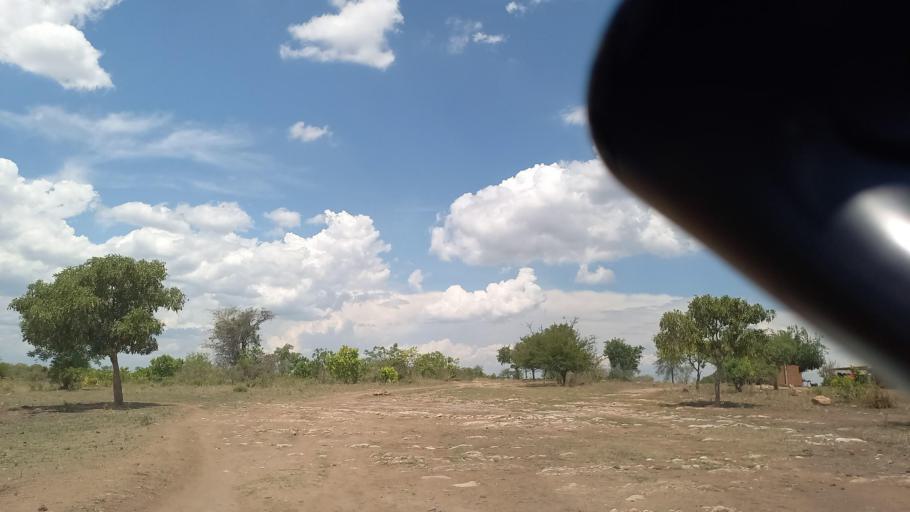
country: ZM
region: Southern
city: Mazabuka
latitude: -16.1101
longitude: 27.8169
